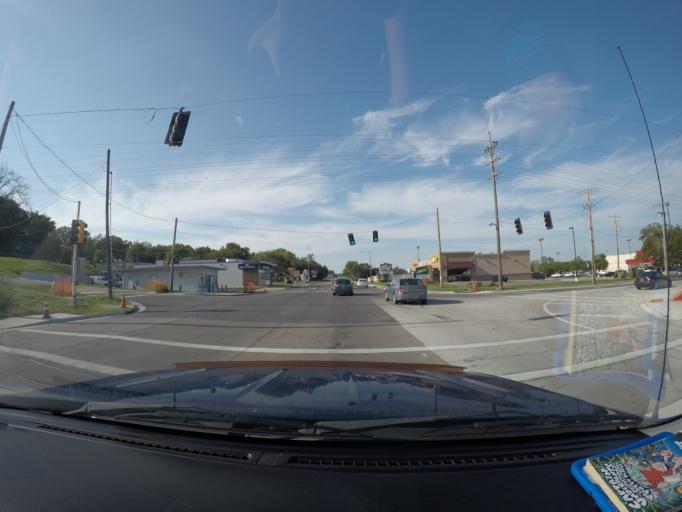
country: US
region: Kansas
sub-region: Leavenworth County
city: Leavenworth
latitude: 39.2949
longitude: -94.9089
